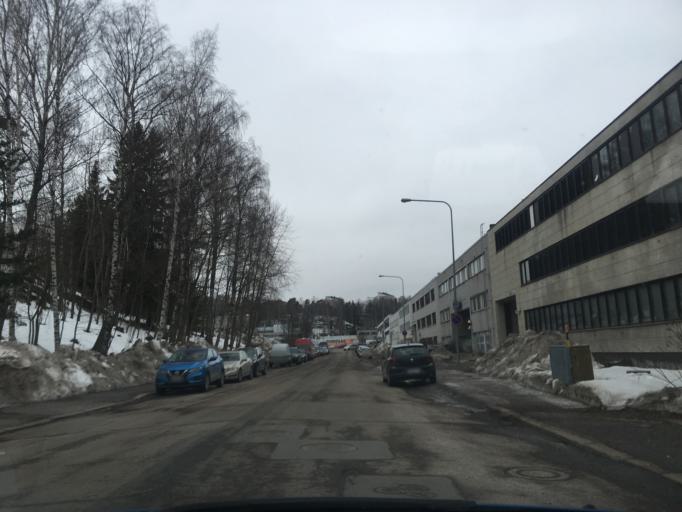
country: FI
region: Uusimaa
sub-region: Helsinki
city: Vantaa
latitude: 60.2100
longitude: 25.0518
